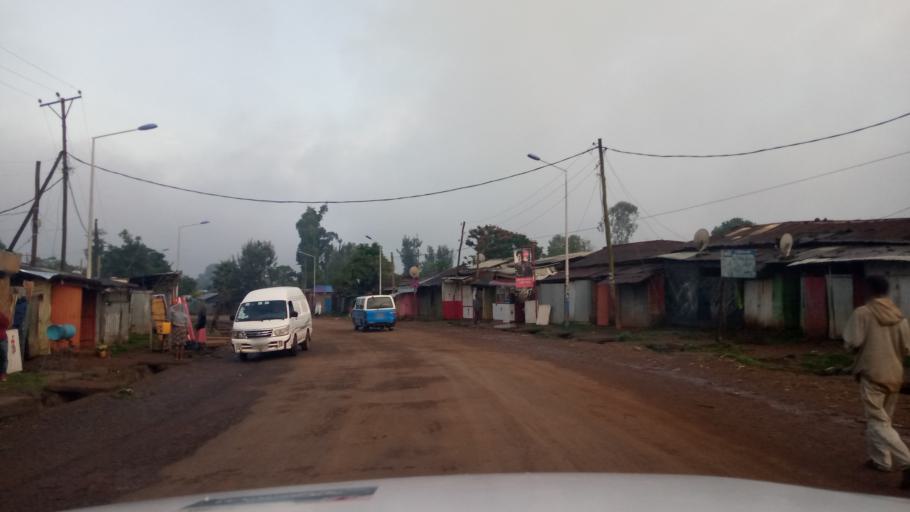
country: ET
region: Oromiya
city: Jima
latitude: 7.6845
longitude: 36.8489
